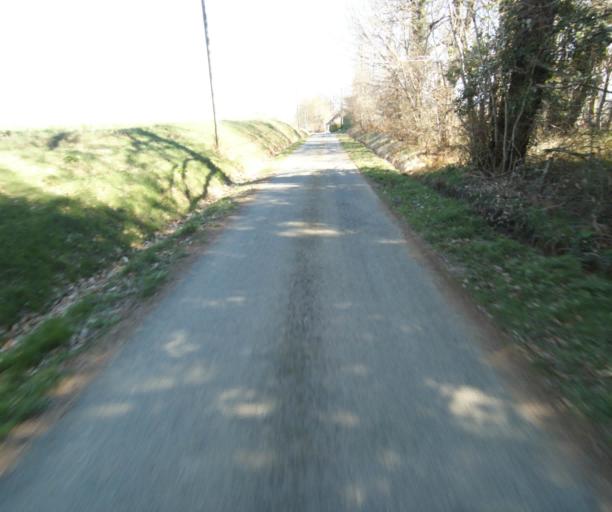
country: FR
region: Limousin
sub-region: Departement de la Correze
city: Seilhac
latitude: 45.4002
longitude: 1.7342
